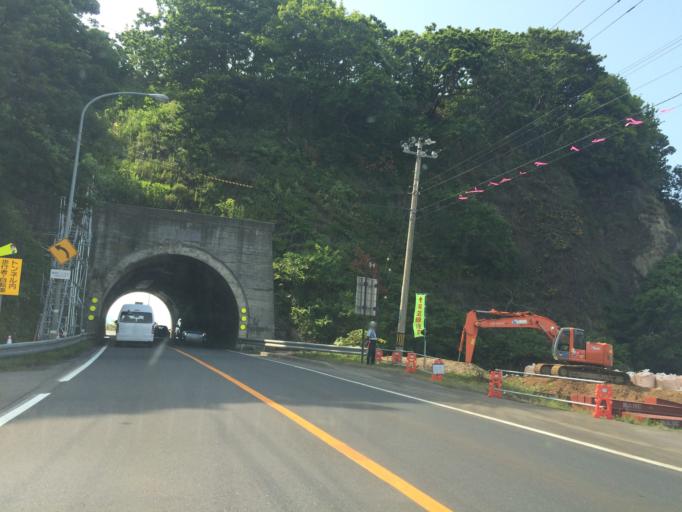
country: JP
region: Hokkaido
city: Yoichi
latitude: 43.1977
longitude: 140.8469
